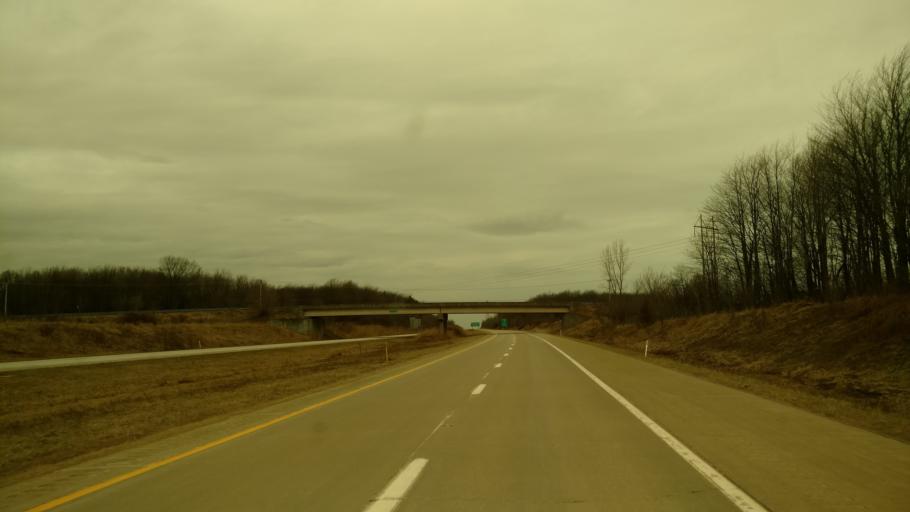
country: US
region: Pennsylvania
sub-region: Erie County
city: North East
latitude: 42.1502
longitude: -79.8611
